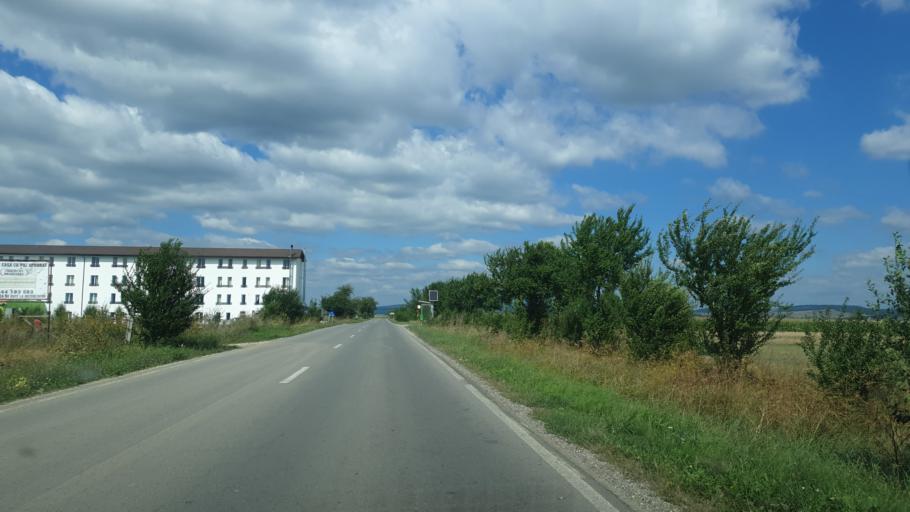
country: RO
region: Brasov
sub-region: Comuna Sanpetru
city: Sanpetru
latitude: 45.7278
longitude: 25.6281
